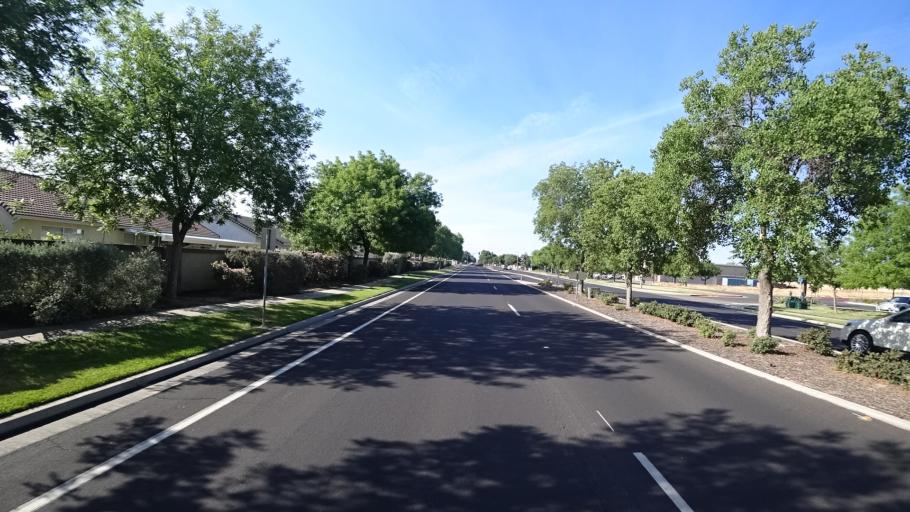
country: US
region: California
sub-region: Kings County
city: Hanford
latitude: 36.3589
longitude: -119.6369
